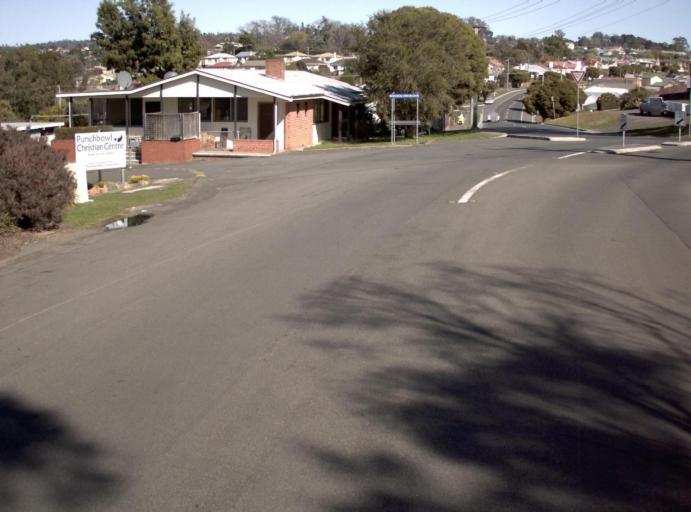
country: AU
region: Tasmania
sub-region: Launceston
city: East Launceston
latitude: -41.4571
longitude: 147.1655
